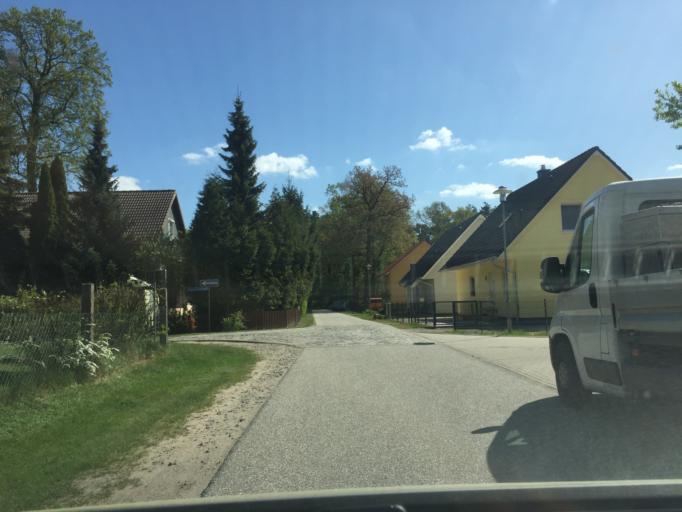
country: DE
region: Mecklenburg-Vorpommern
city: Torgelow
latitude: 53.6400
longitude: 14.0379
